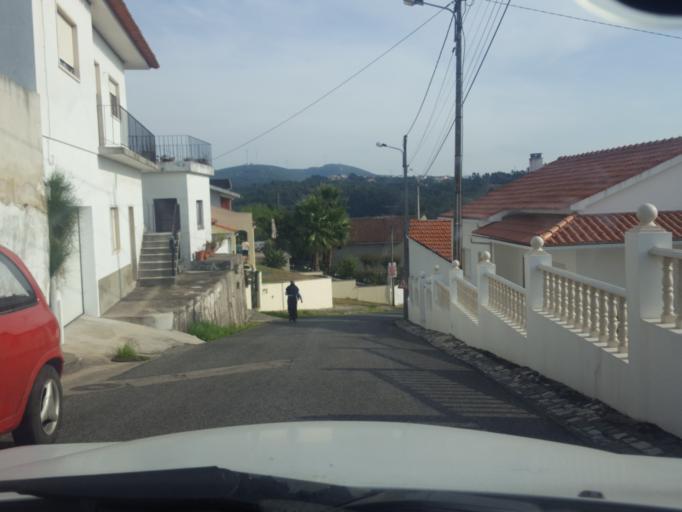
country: PT
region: Leiria
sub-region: Leiria
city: Leiria
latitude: 39.7226
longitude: -8.7809
